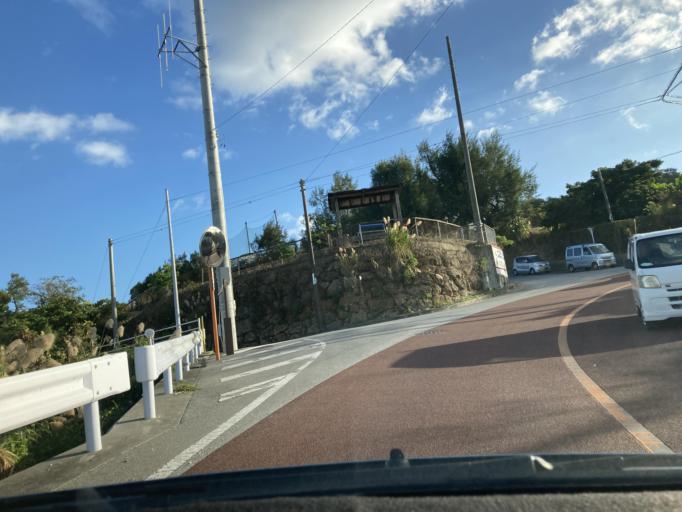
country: JP
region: Okinawa
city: Chatan
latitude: 26.2947
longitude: 127.8000
